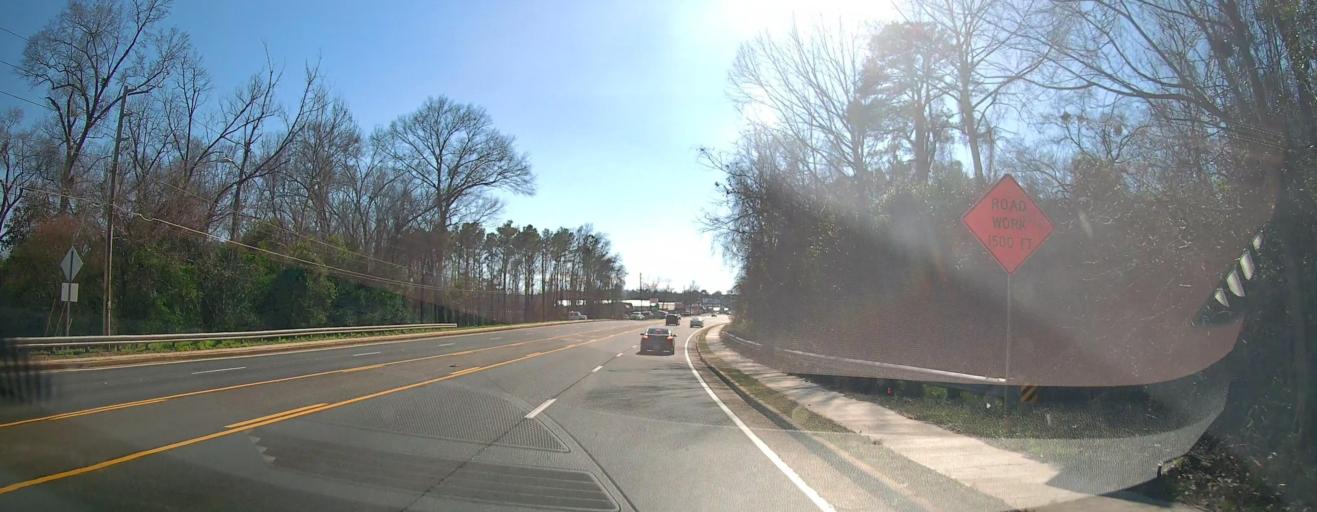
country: US
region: Georgia
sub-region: Sumter County
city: Americus
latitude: 32.0785
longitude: -84.2391
